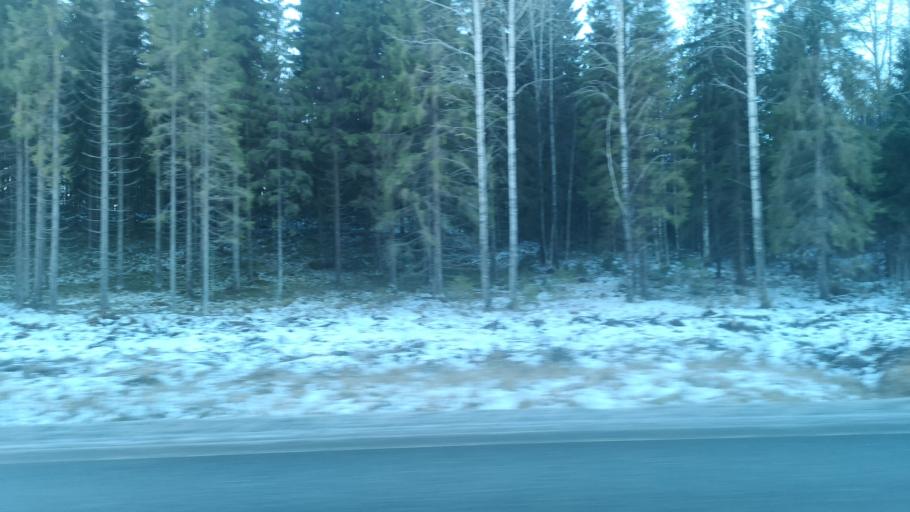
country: FI
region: Southern Savonia
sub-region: Pieksaemaeki
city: Juva
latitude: 61.7896
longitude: 27.5972
